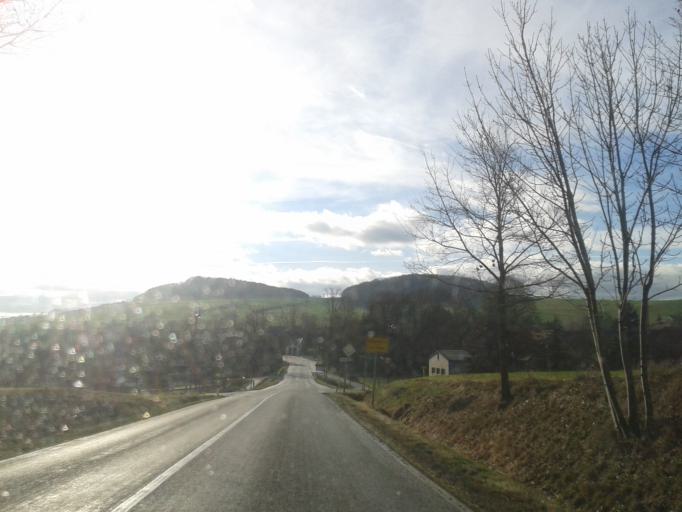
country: DE
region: Saxony
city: Eibau
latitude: 50.9785
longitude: 14.6974
